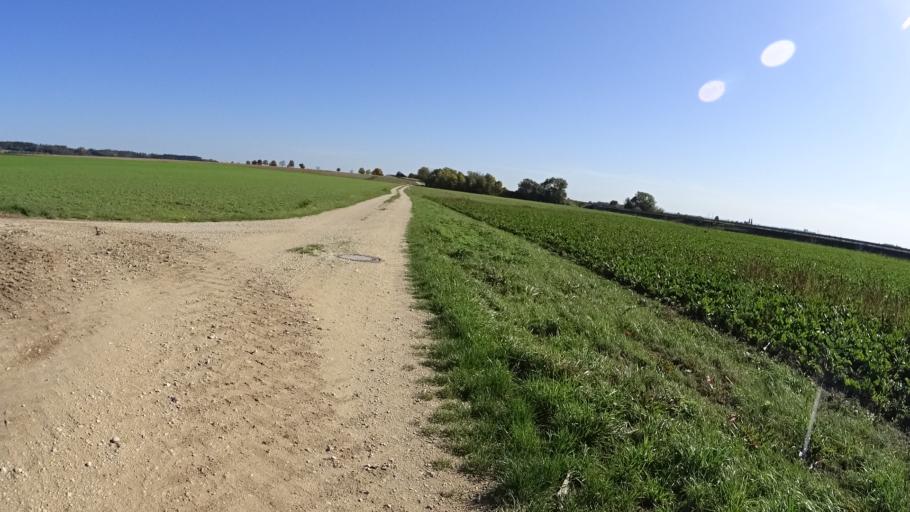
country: DE
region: Bavaria
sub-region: Upper Bavaria
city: Gaimersheim
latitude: 48.8268
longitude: 11.3581
